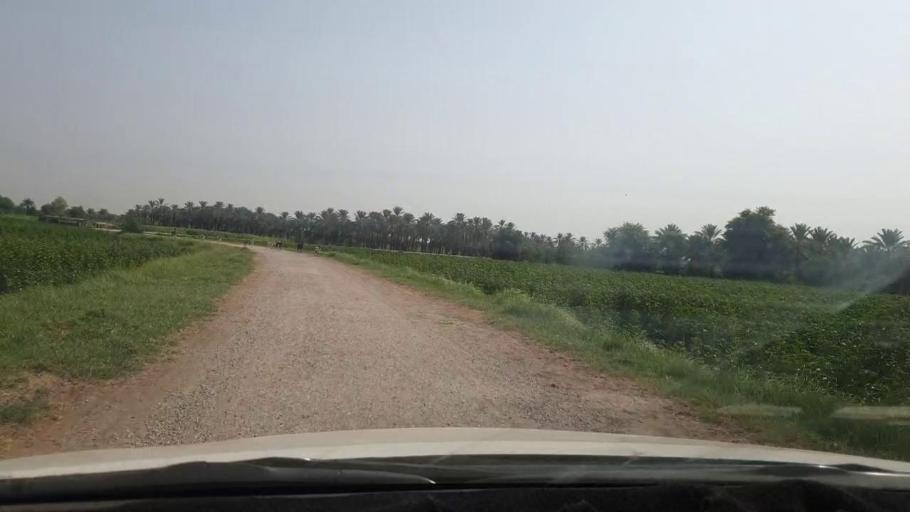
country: PK
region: Sindh
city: Rohri
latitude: 27.6096
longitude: 68.8925
